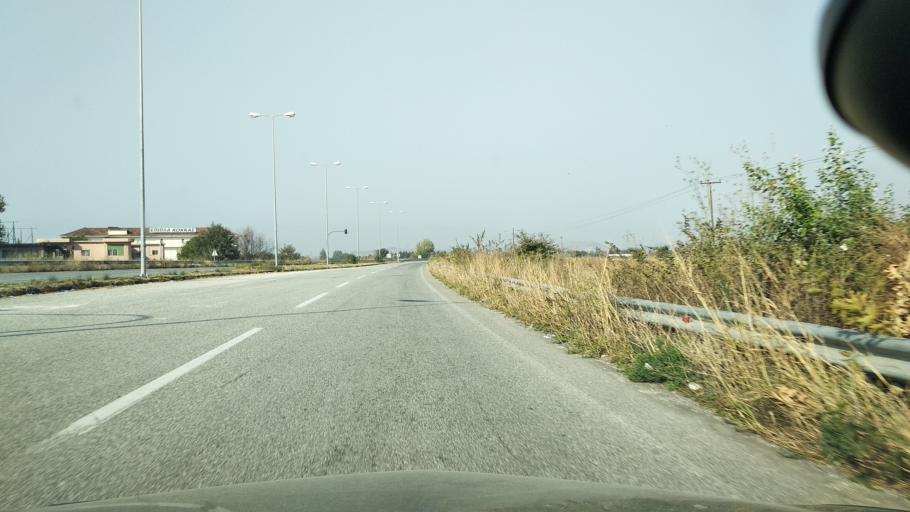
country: GR
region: Thessaly
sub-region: Trikala
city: Megalochori
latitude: 39.5624
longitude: 21.8574
